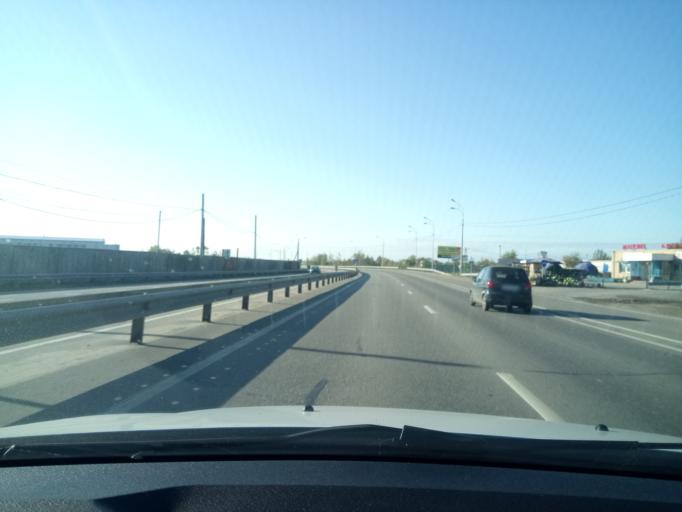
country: RU
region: Nizjnij Novgorod
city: Burevestnik
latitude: 56.1607
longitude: 43.9129
